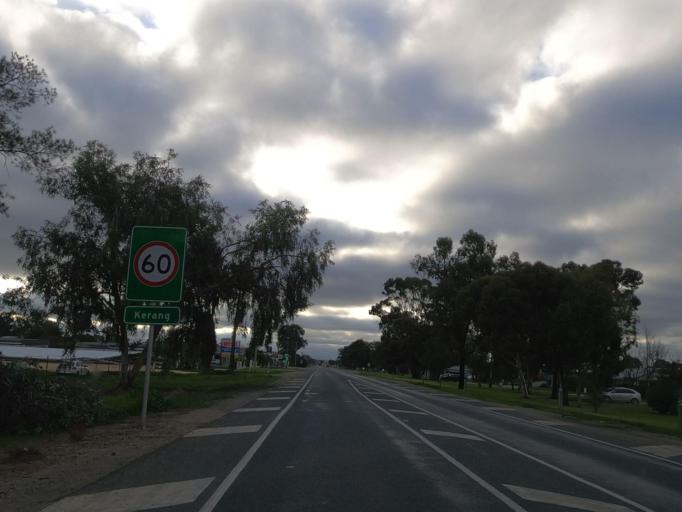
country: AU
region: Victoria
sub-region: Swan Hill
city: Swan Hill
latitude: -35.7418
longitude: 143.9203
